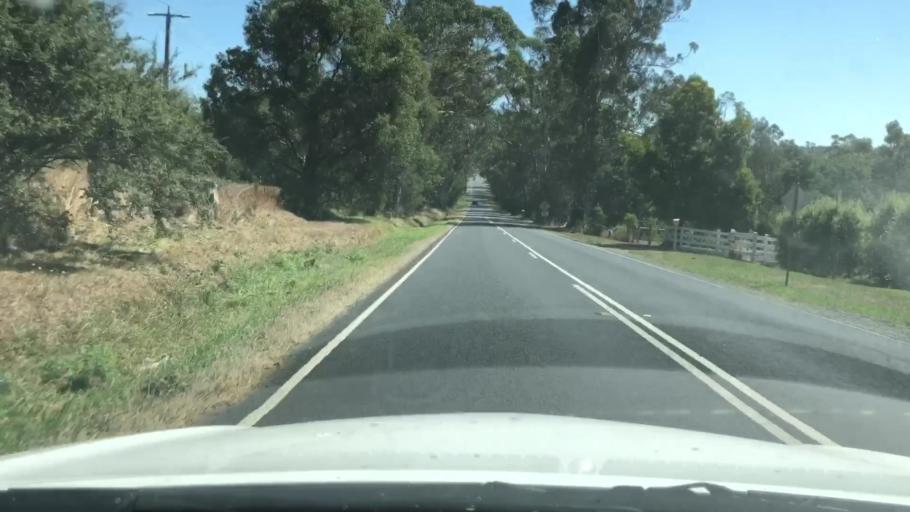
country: AU
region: Victoria
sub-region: Yarra Ranges
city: Woori Yallock
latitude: -37.8065
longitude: 145.5178
